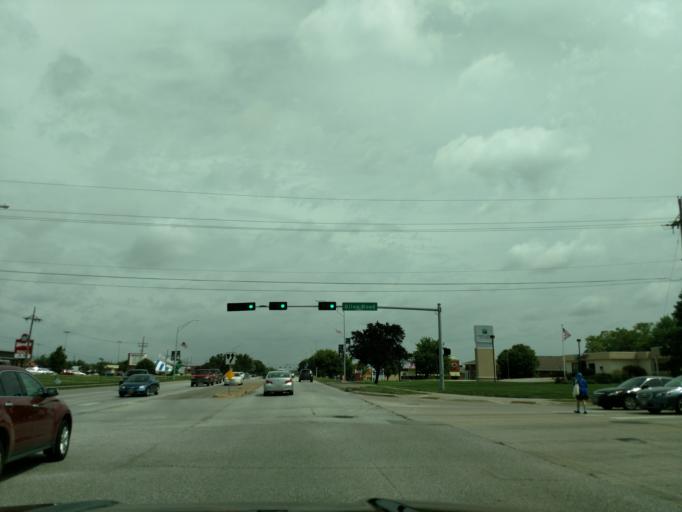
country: US
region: Nebraska
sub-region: Sarpy County
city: La Vista
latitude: 41.1759
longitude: -96.0429
